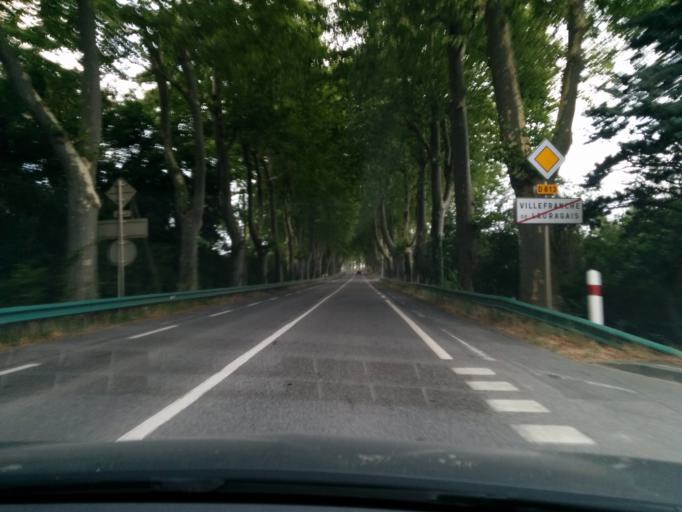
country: FR
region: Midi-Pyrenees
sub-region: Departement de la Haute-Garonne
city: Villefranche-de-Lauragais
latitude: 43.4089
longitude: 1.7064
